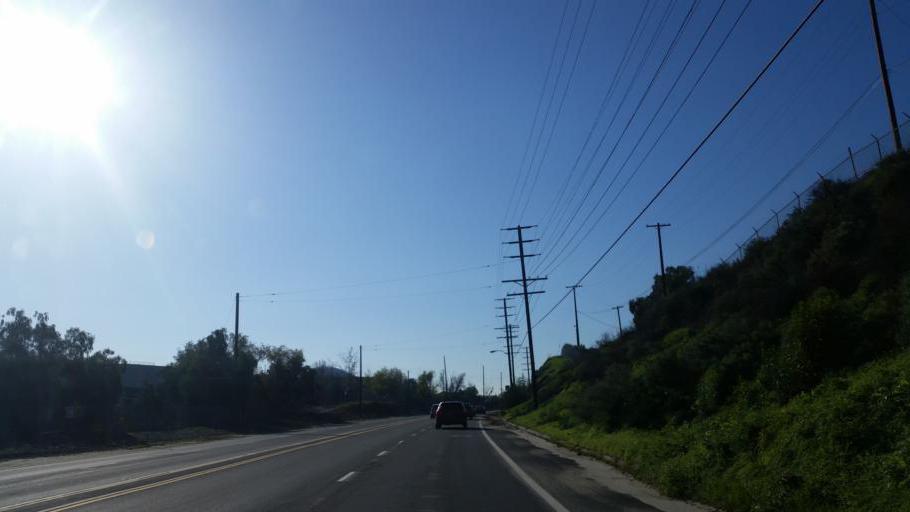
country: US
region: California
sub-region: Los Angeles County
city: Lomita
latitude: 33.7709
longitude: -118.2944
